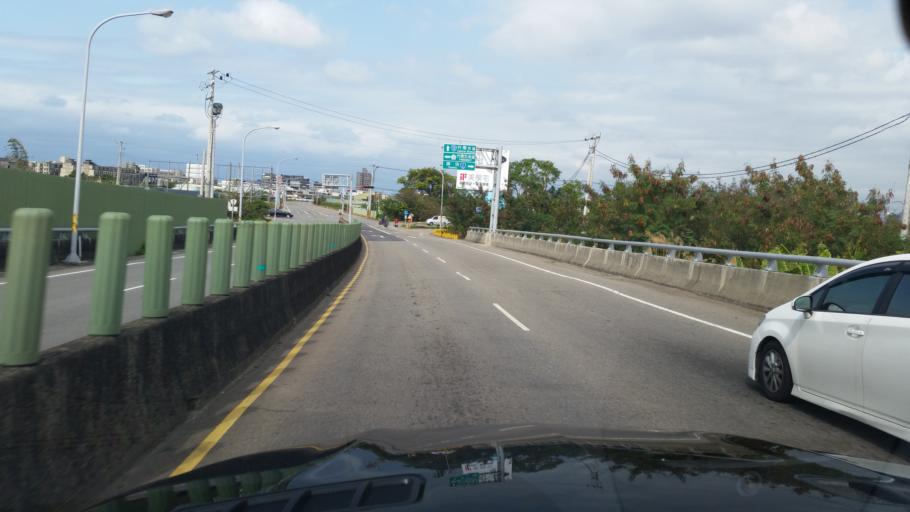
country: TW
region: Taiwan
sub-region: Miaoli
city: Miaoli
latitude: 24.6693
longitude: 120.8673
